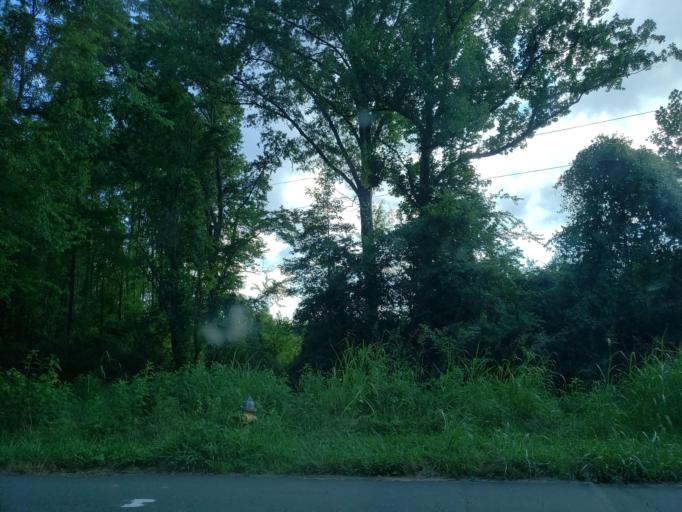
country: US
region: Georgia
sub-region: Bartow County
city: Rydal
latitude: 34.2781
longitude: -84.8007
